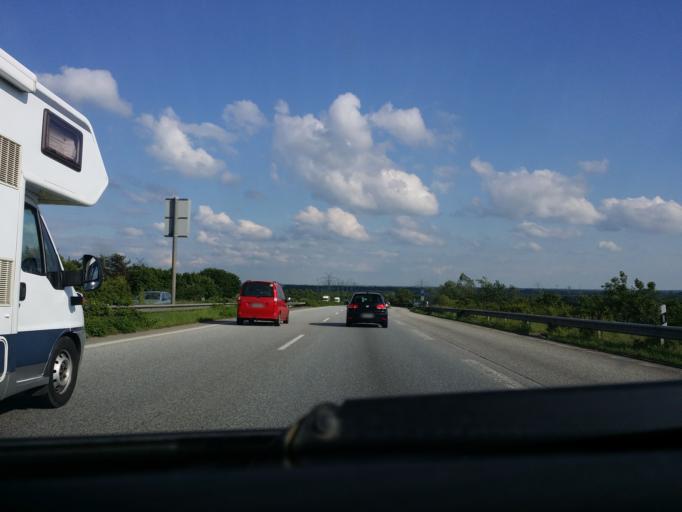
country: DE
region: Schleswig-Holstein
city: Borgstedt
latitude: 54.3273
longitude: 9.7321
